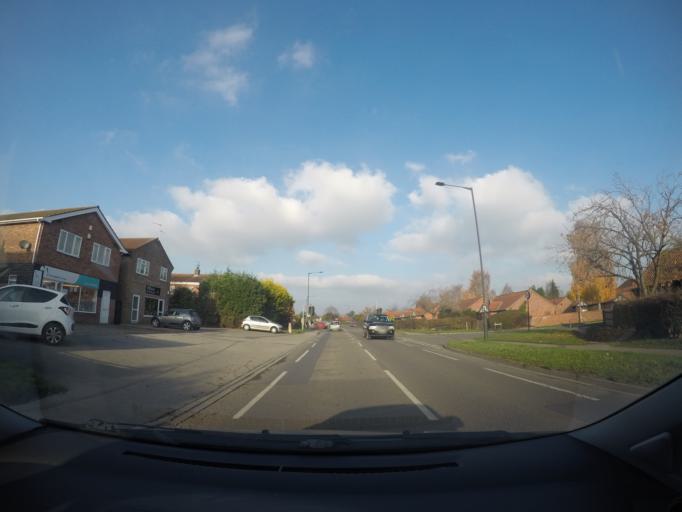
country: GB
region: England
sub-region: City of York
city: Huntington
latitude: 53.9963
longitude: -1.0574
